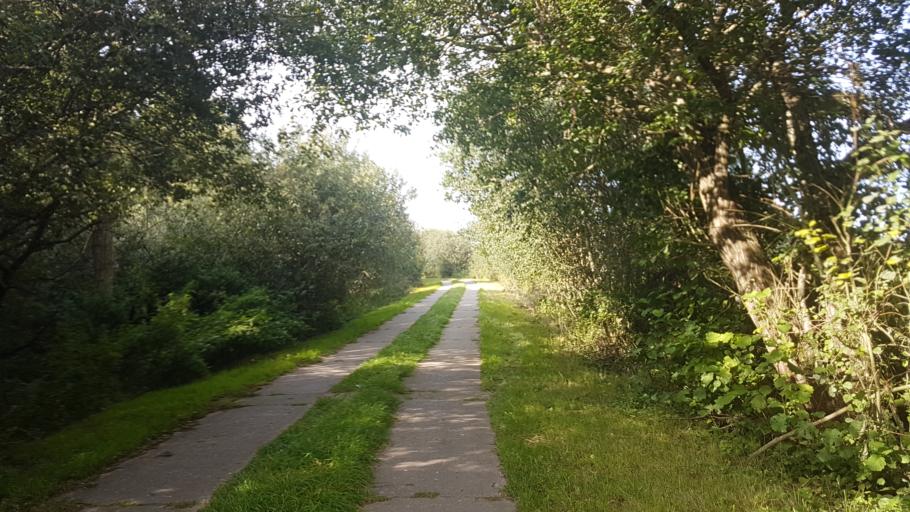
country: DE
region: Mecklenburg-Vorpommern
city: Gingst
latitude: 54.4368
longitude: 13.1960
